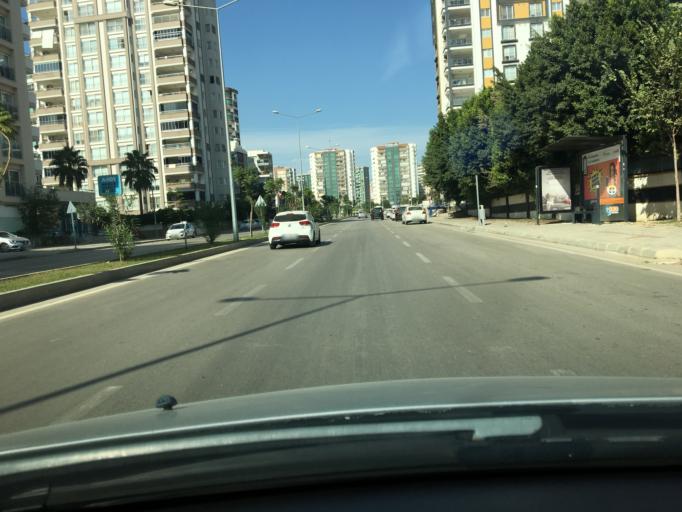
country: TR
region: Adana
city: Seyhan
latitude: 37.0201
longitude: 35.2584
